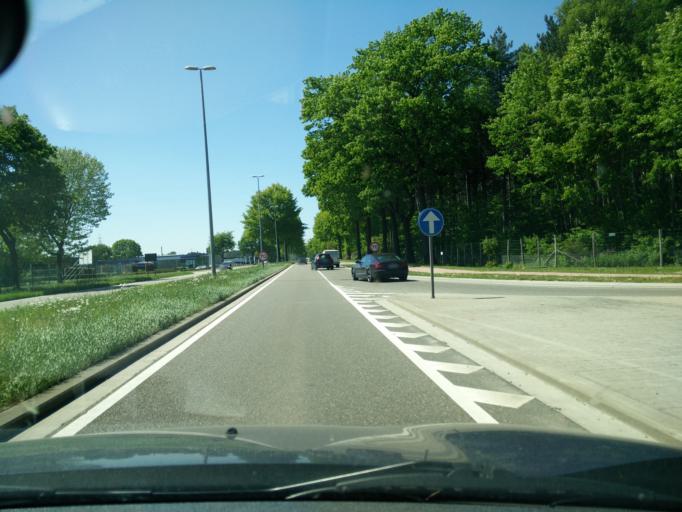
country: BE
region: Flanders
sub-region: Provincie Limburg
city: Maasmechelen
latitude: 51.0180
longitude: 5.7002
